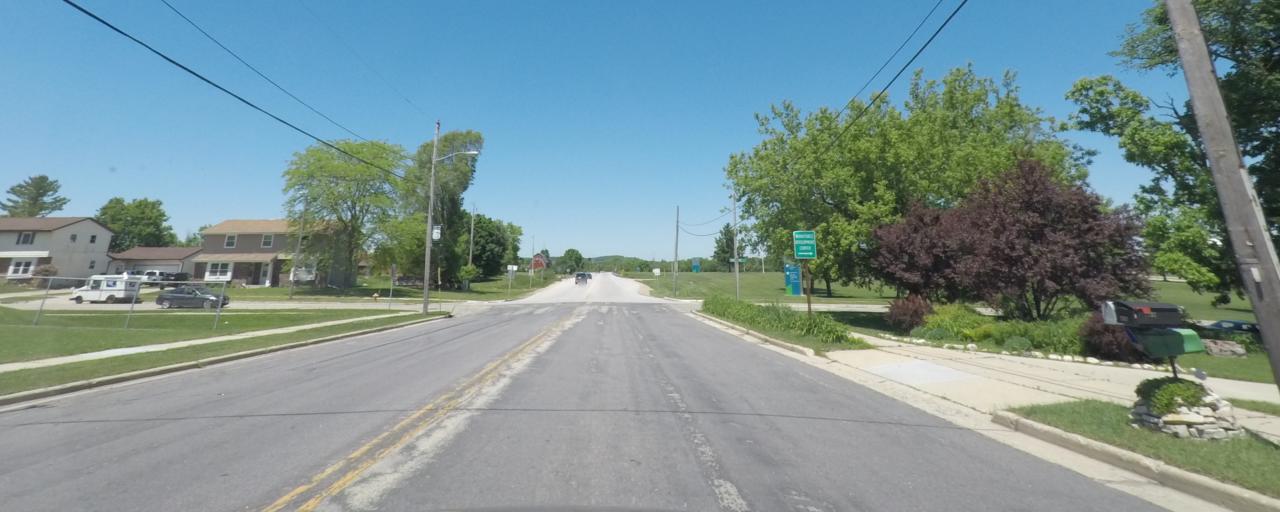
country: US
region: Wisconsin
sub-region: Washington County
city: West Bend
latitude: 43.4465
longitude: -88.1904
